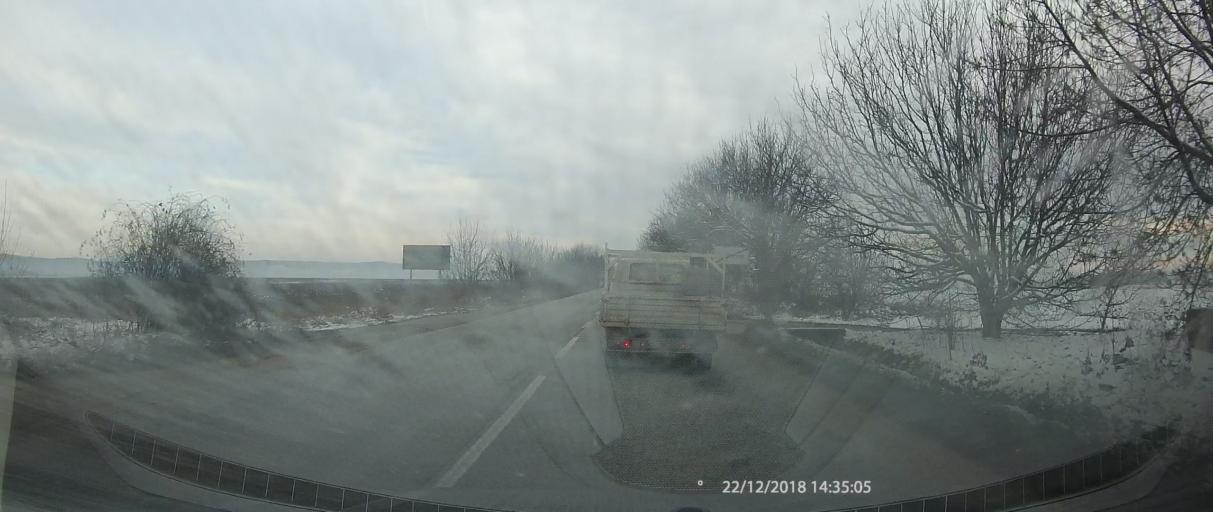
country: BG
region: Pleven
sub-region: Obshtina Levski
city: Levski
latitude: 43.4358
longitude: 25.0882
